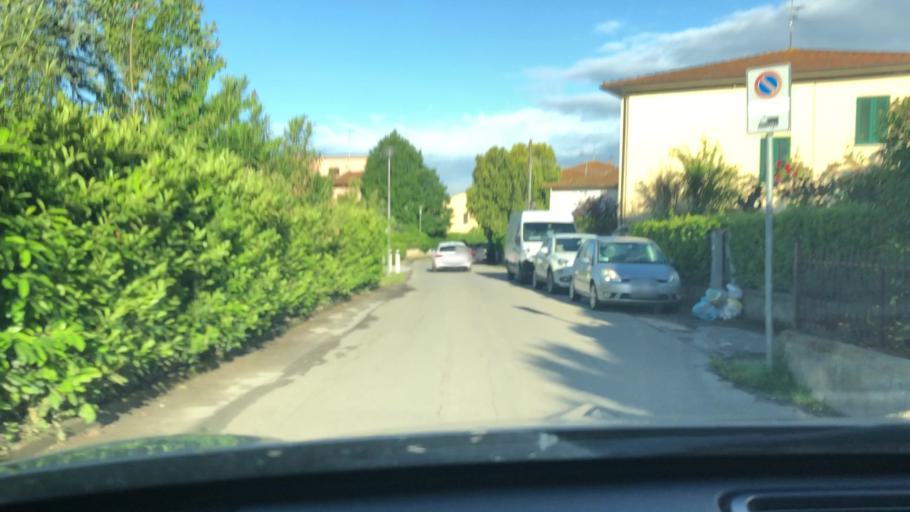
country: IT
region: Tuscany
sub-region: Province of Pisa
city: Forcoli
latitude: 43.6032
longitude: 10.7012
